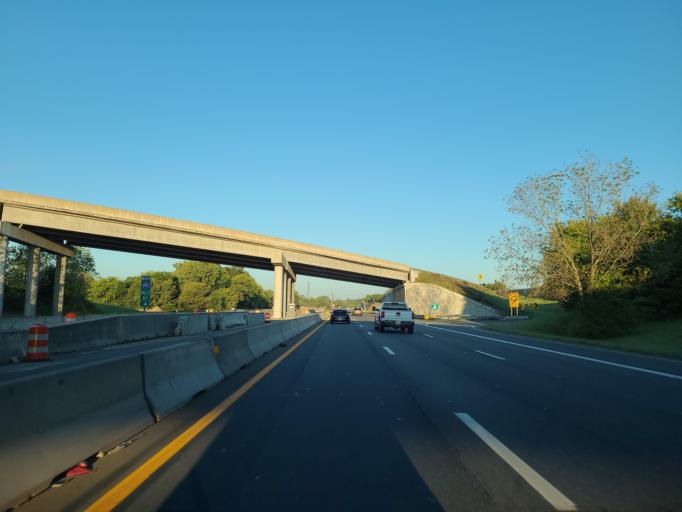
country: US
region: North Carolina
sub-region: Mecklenburg County
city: Pineville
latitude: 35.0653
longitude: -80.8459
